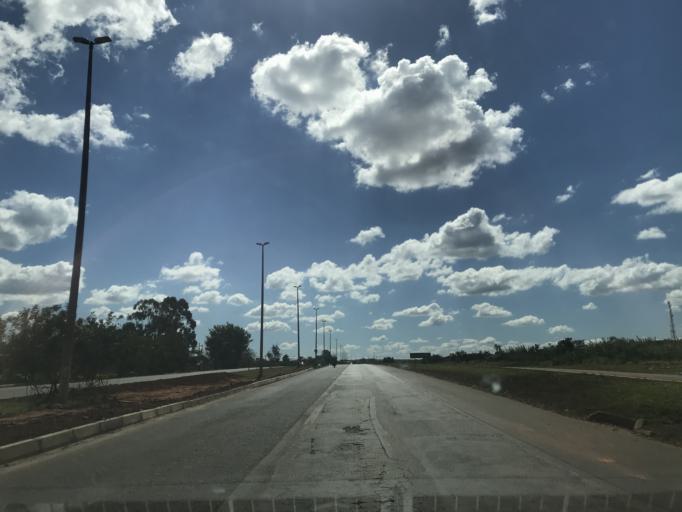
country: BR
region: Federal District
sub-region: Brasilia
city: Brasilia
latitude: -15.8076
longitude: -48.0008
